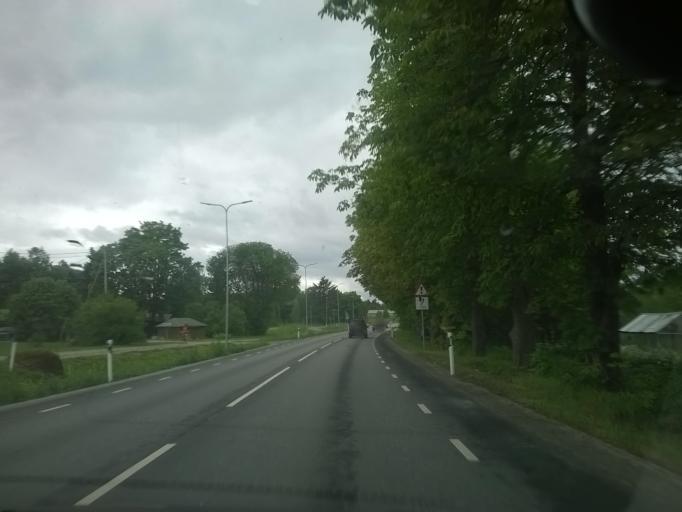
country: EE
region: Harju
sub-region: Rae vald
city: Jueri
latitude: 59.3757
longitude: 24.8529
